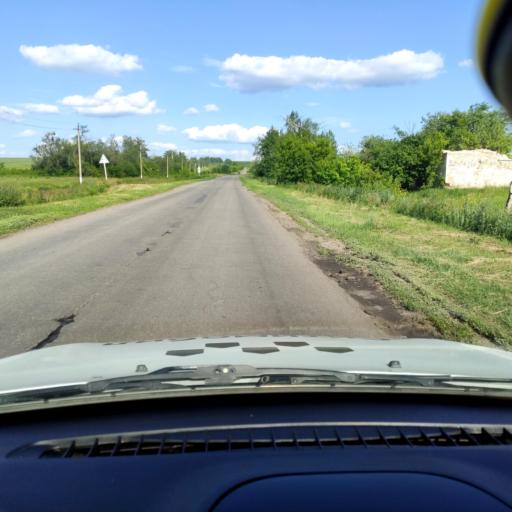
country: RU
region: Samara
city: Zhigulevsk
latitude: 53.3538
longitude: 49.3266
